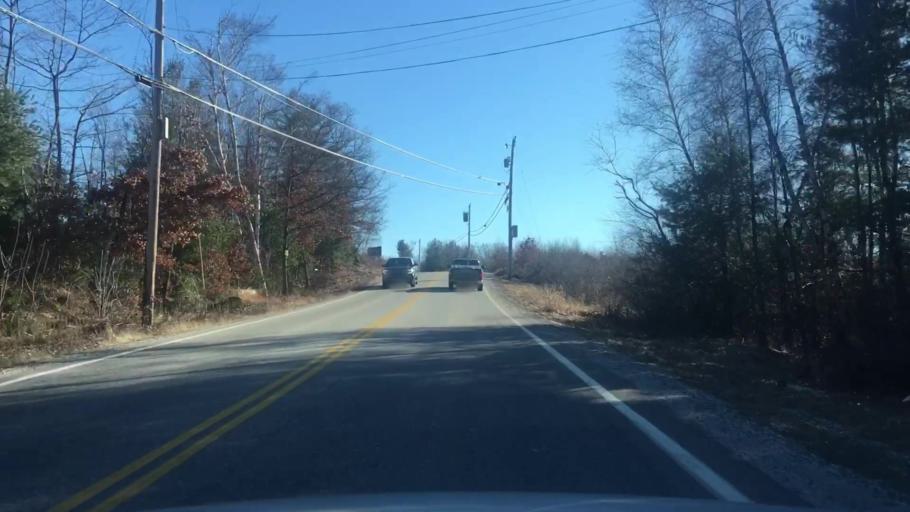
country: US
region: New Hampshire
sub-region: Rockingham County
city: Londonderry
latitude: 42.9060
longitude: -71.4186
